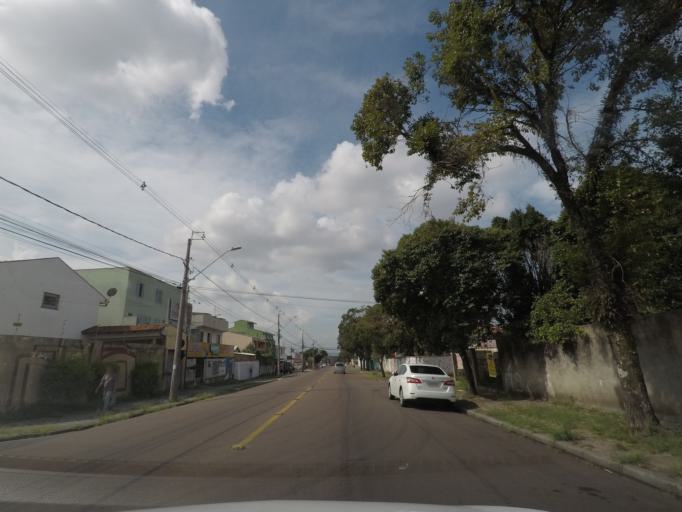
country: BR
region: Parana
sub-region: Pinhais
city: Pinhais
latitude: -25.4706
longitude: -49.2102
